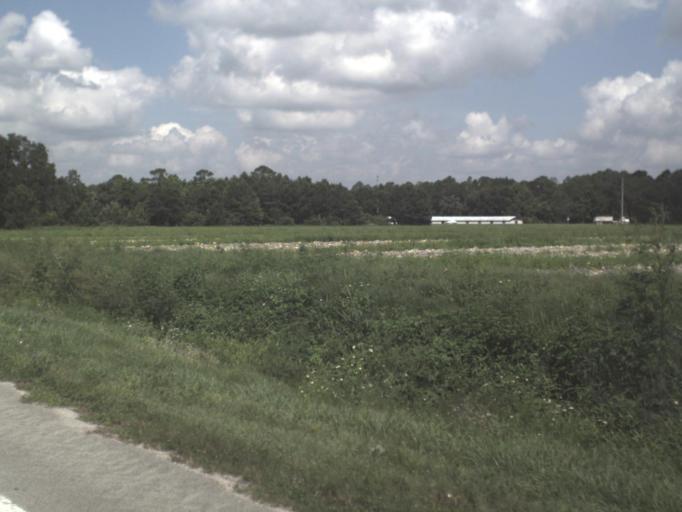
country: US
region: Florida
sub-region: Putnam County
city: East Palatka
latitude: 29.7256
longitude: -81.4772
